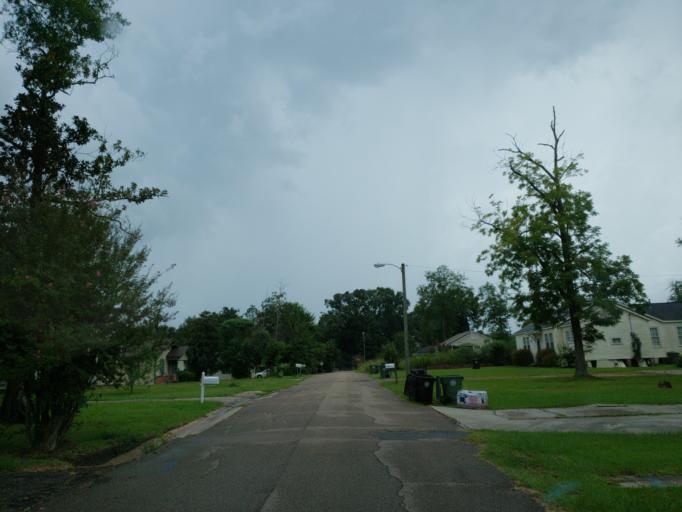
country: US
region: Mississippi
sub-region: Forrest County
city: Hattiesburg
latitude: 31.3277
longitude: -89.3252
